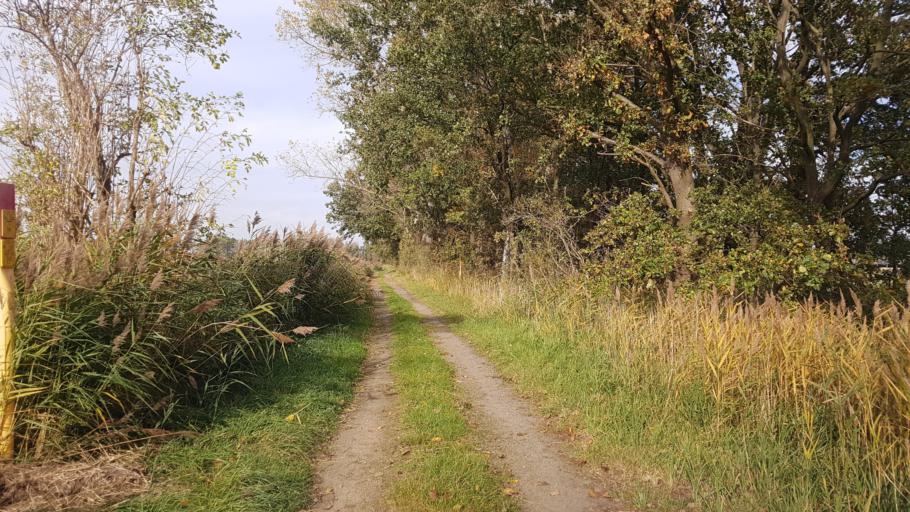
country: DE
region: Brandenburg
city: Schraden
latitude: 51.4536
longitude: 13.6994
